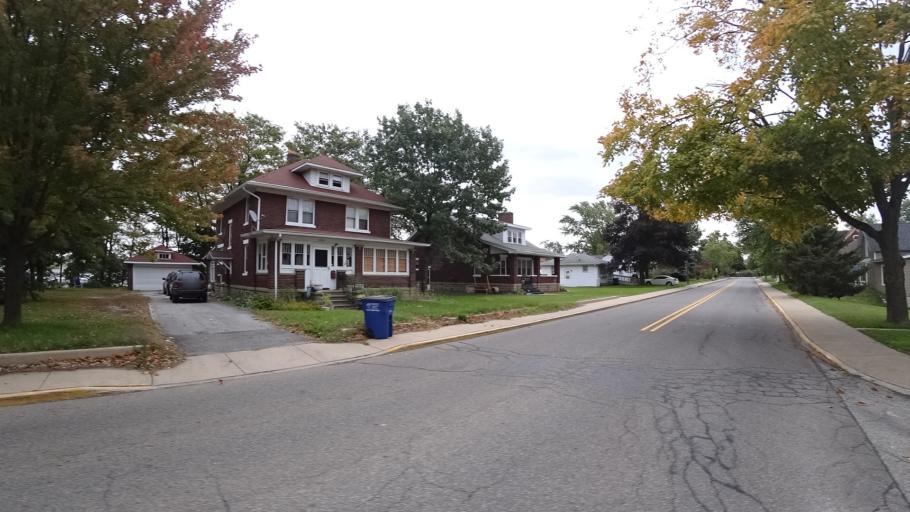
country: US
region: Indiana
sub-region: LaPorte County
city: Michigan City
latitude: 41.6999
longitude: -86.8966
